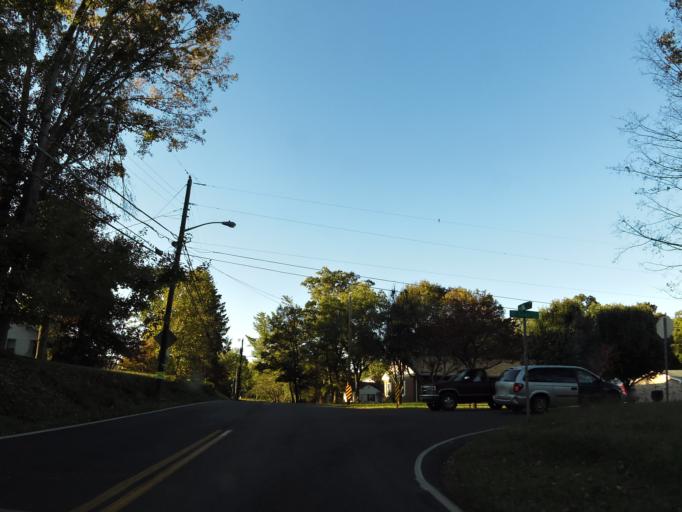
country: US
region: Tennessee
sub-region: Knox County
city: Knoxville
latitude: 36.0144
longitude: -83.9515
